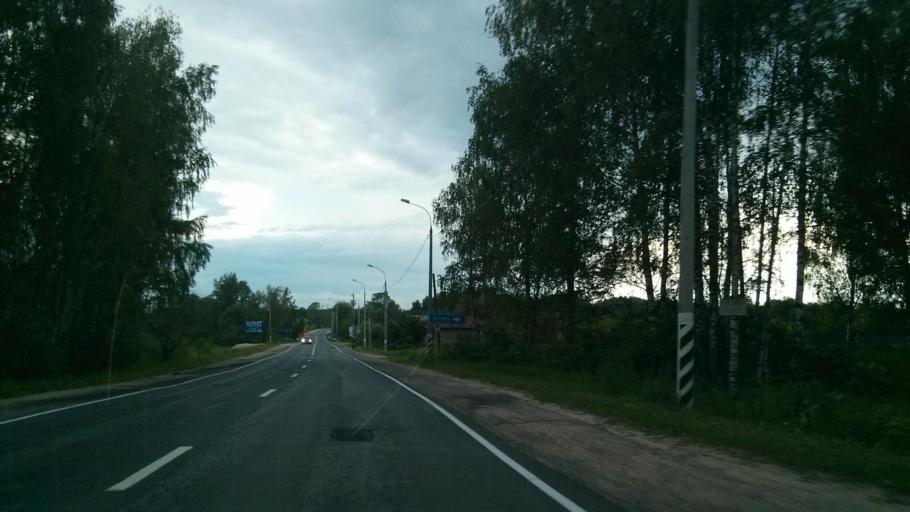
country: RU
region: Nizjnij Novgorod
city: Vacha
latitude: 55.7577
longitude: 42.5221
